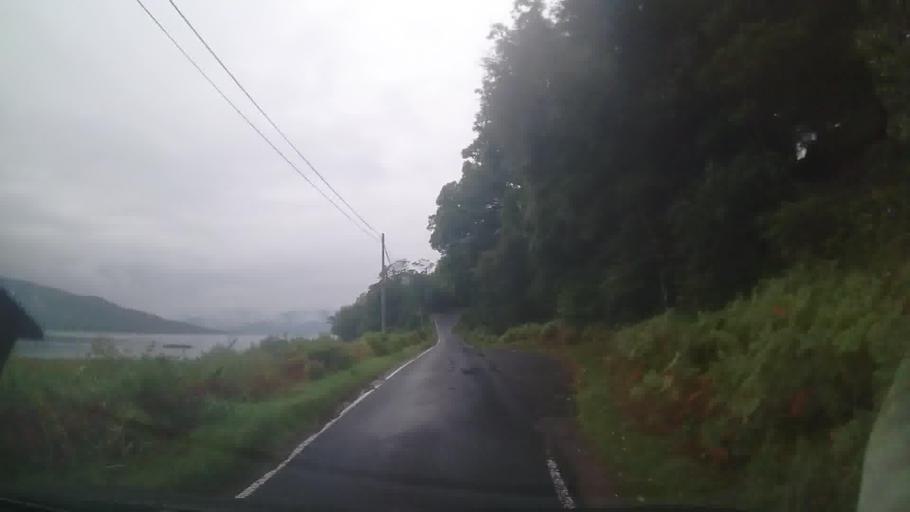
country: GB
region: Scotland
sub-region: Argyll and Bute
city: Isle Of Mull
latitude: 56.7036
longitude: -5.7047
